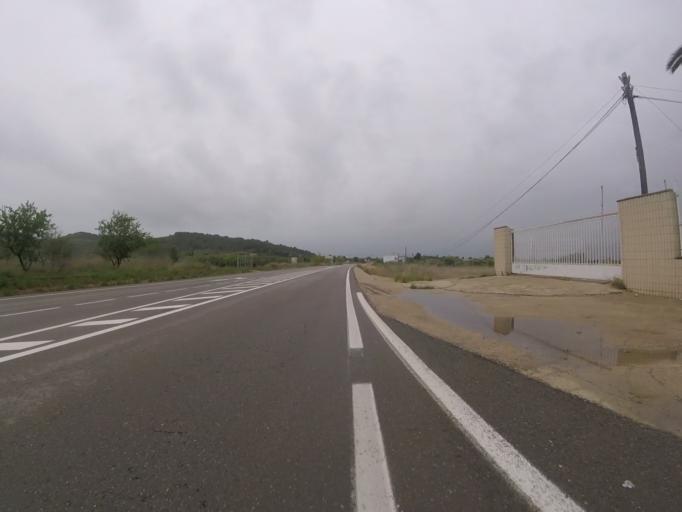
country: ES
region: Valencia
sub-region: Provincia de Castello
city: Alcoceber
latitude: 40.2557
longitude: 0.2451
